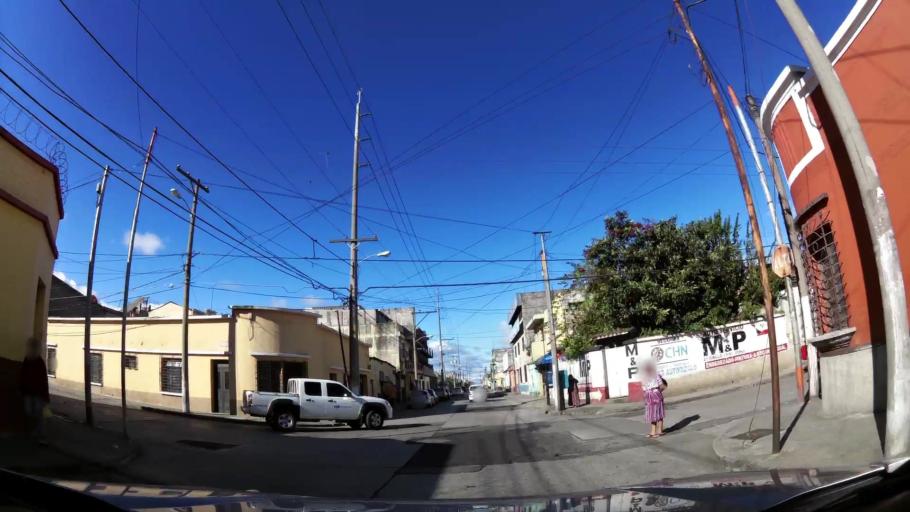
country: GT
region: Guatemala
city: Guatemala City
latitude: 14.6279
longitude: -90.5074
